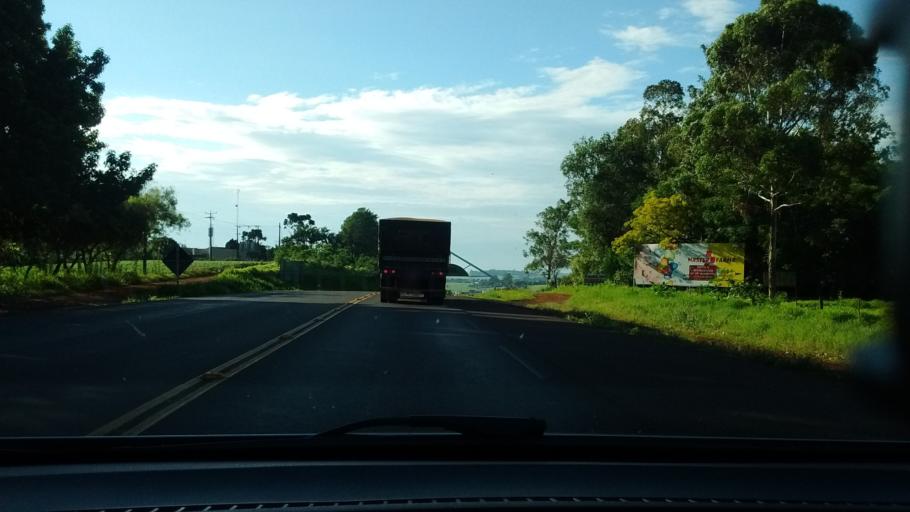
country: BR
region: Parana
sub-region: Cascavel
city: Cascavel
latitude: -25.2511
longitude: -53.5784
